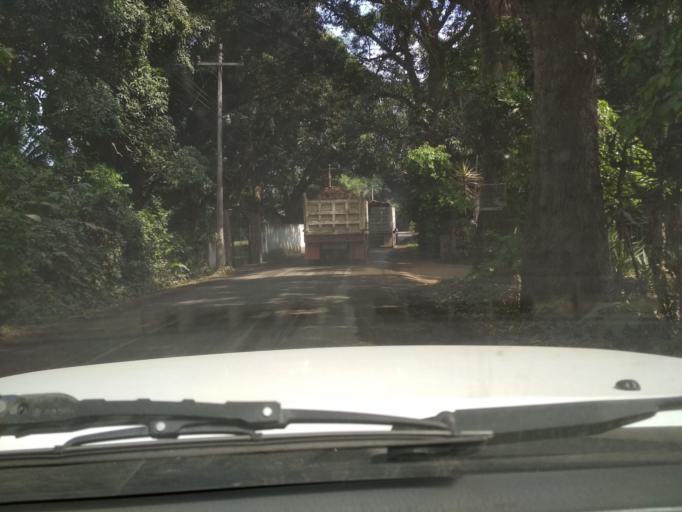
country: MX
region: Veracruz
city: El Tejar
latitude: 19.0813
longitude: -96.1722
